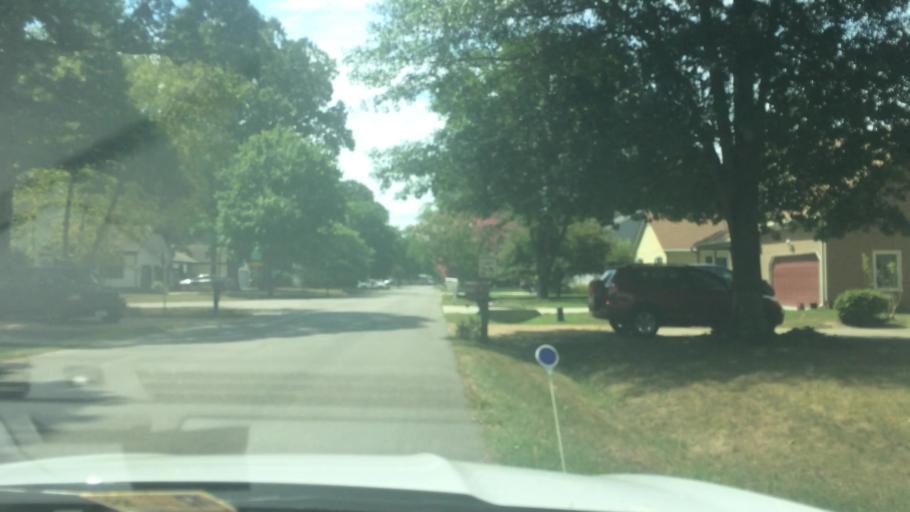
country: US
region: Virginia
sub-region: City of Poquoson
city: Poquoson
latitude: 37.1158
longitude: -76.4519
